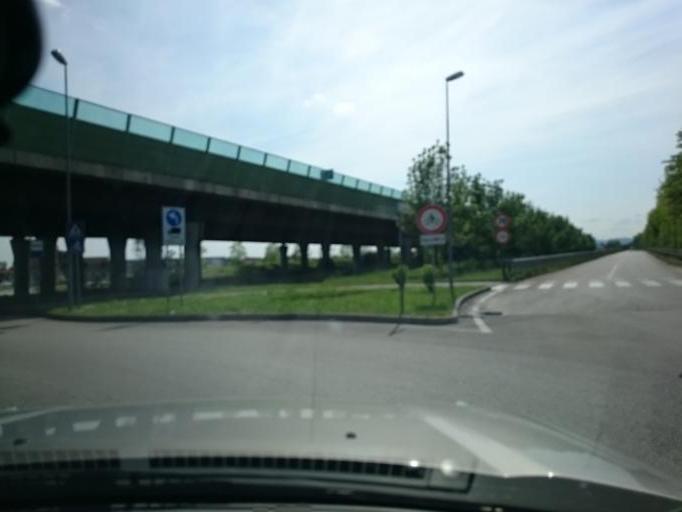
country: IT
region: Veneto
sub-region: Provincia di Padova
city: Mandriola-Sant'Agostino
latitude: 45.3648
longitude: 11.8713
